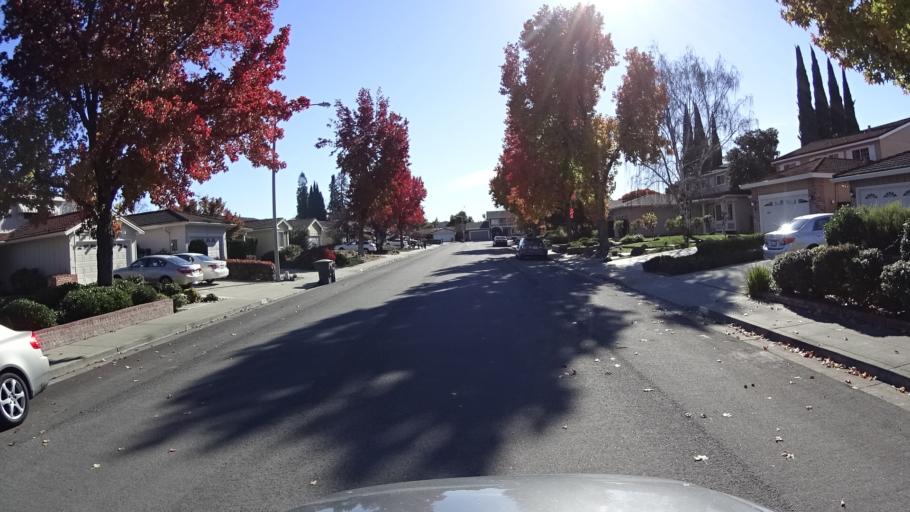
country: US
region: California
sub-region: Santa Clara County
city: Sunnyvale
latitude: 37.3651
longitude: -122.0042
